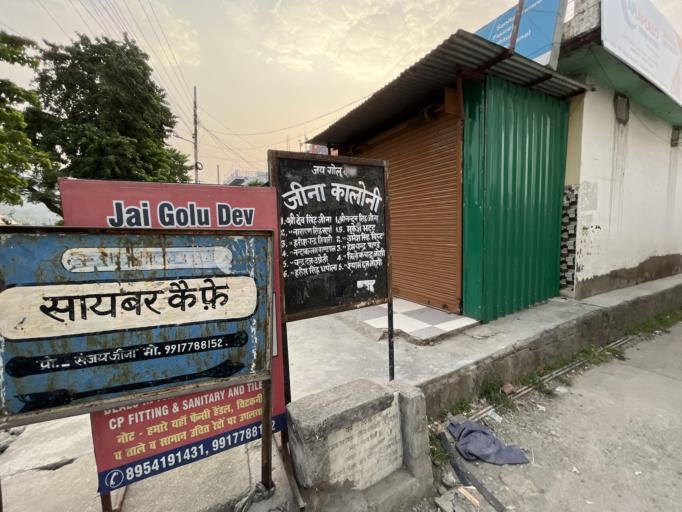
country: IN
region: Uttarakhand
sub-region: Naini Tal
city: Haldwani
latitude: 29.2329
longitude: 79.5080
